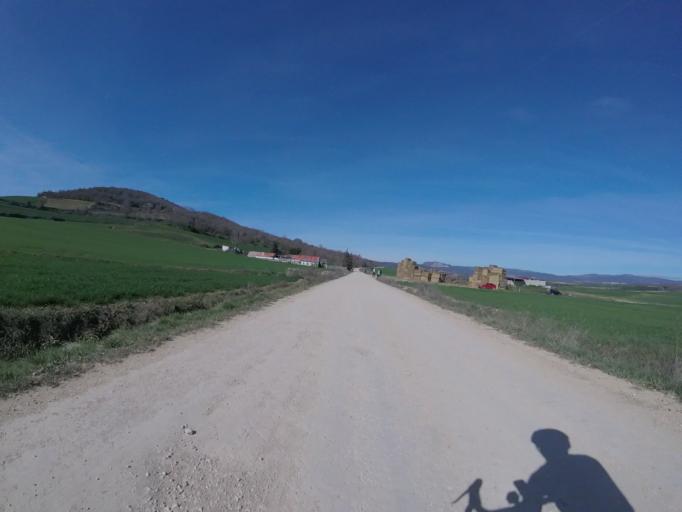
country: ES
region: Navarre
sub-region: Provincia de Navarra
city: Villatuerta
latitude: 42.6515
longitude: -1.9726
